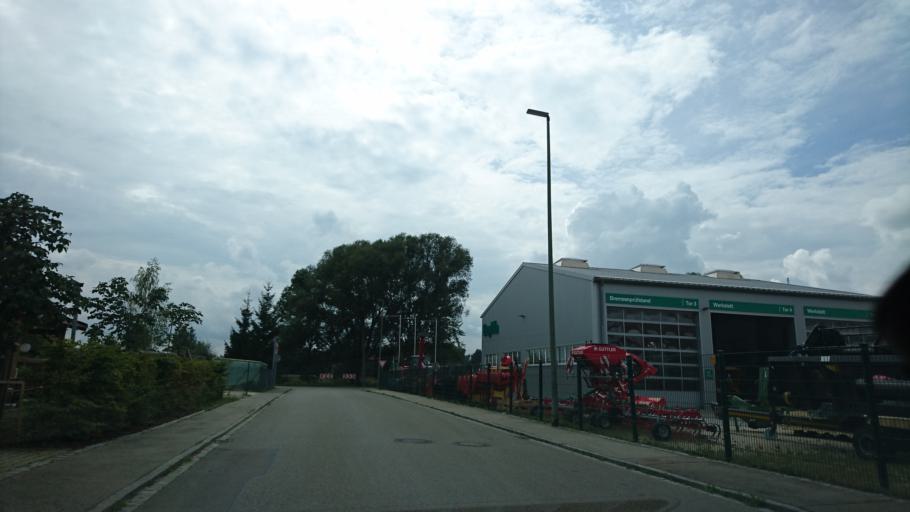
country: DE
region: Bavaria
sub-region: Swabia
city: Dinkelscherben
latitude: 48.3449
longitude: 10.5945
